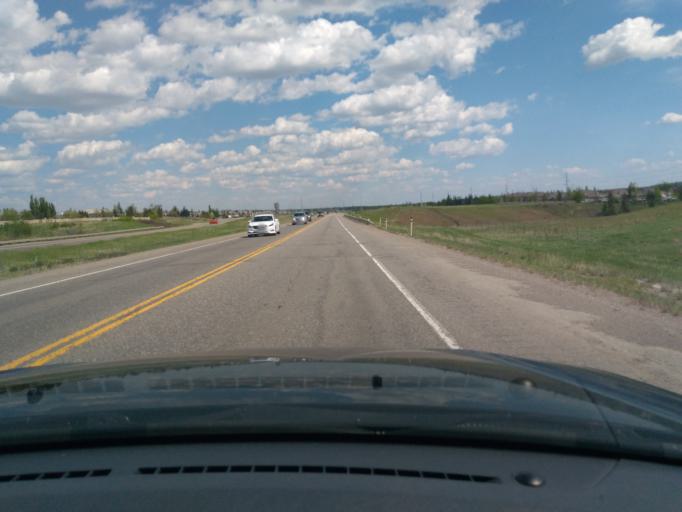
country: CA
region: Alberta
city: Calgary
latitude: 51.0191
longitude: -114.2092
